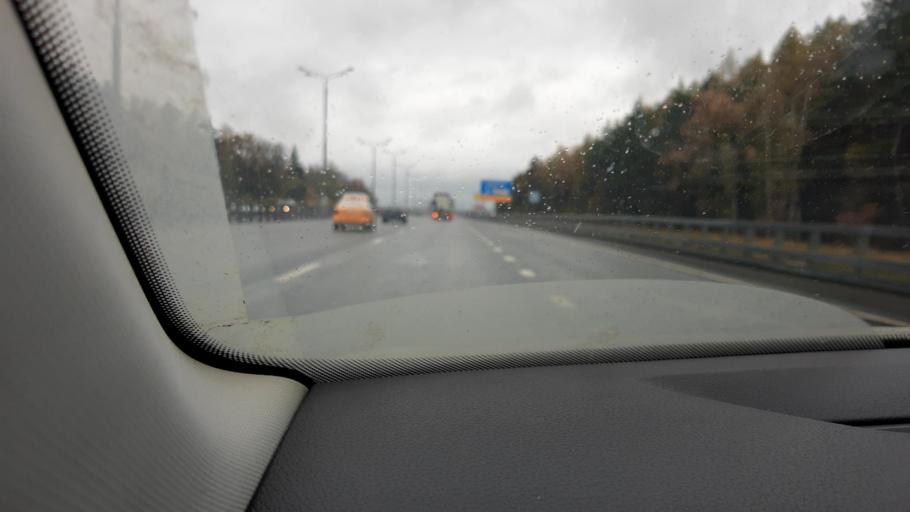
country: RU
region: Moskovskaya
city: Aprelevka
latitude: 55.5425
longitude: 37.0944
